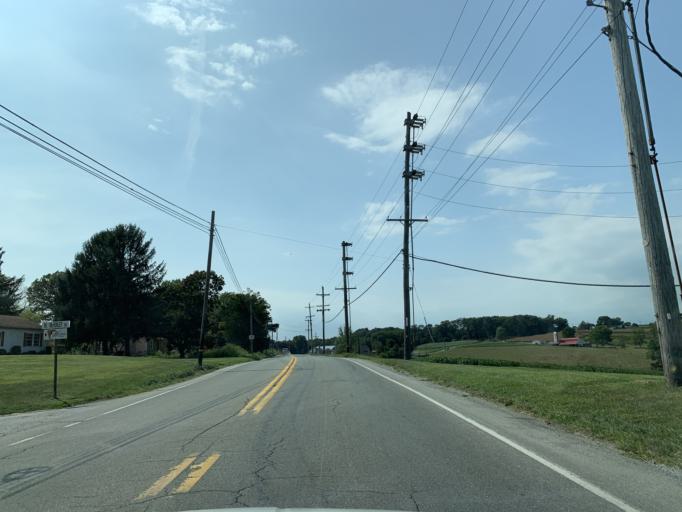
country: US
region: Pennsylvania
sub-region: York County
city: Susquehanna Trails
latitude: 39.7742
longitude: -76.3415
